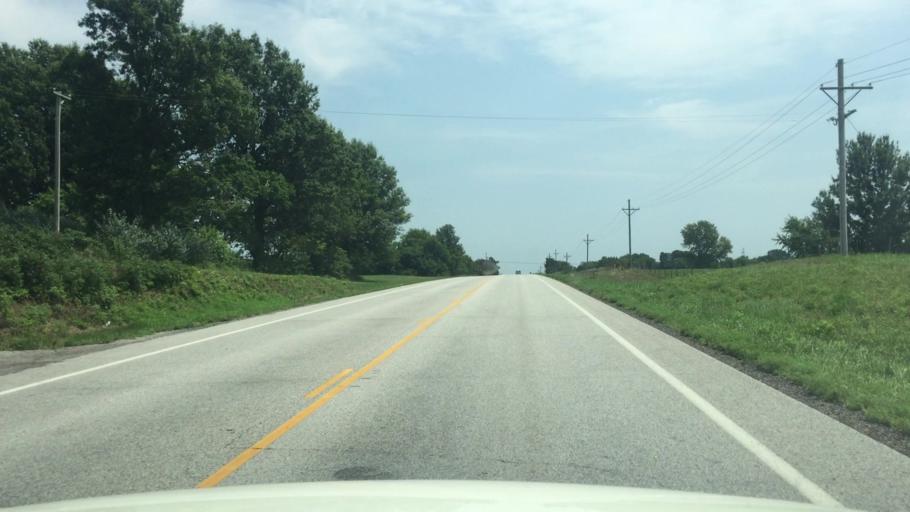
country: US
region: Kansas
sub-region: Cherokee County
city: Columbus
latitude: 37.1780
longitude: -94.7891
